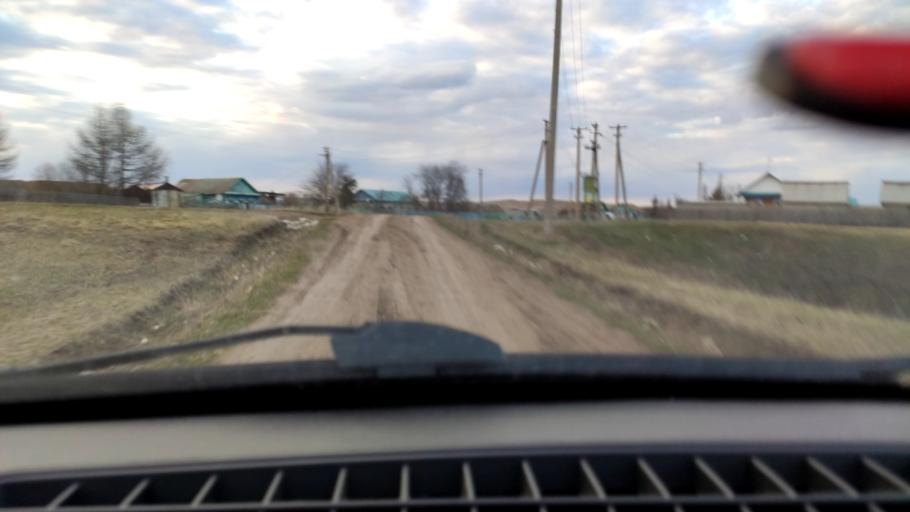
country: RU
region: Bashkortostan
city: Tolbazy
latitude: 54.0170
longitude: 55.5327
